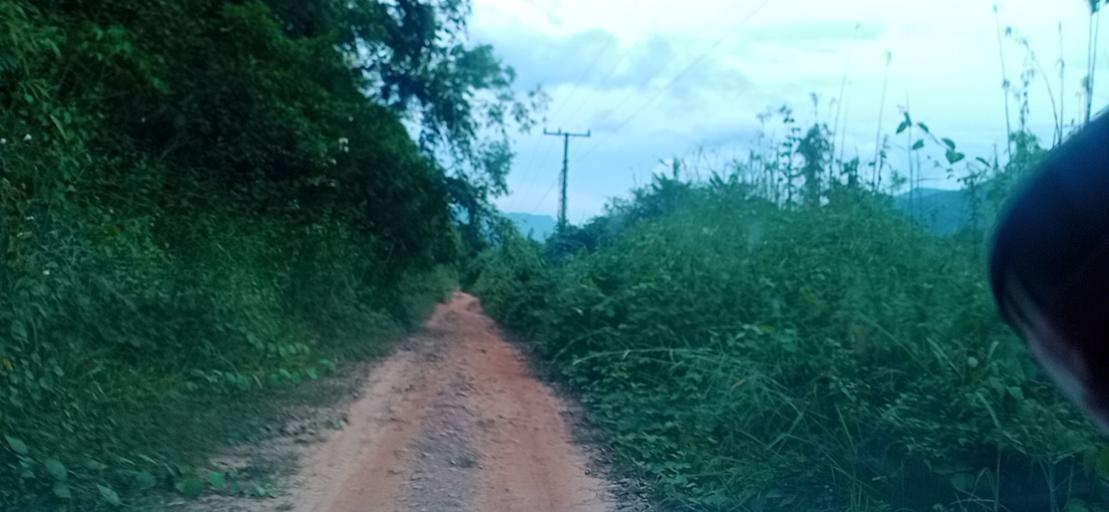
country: TH
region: Changwat Bueng Kan
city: Pak Khat
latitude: 18.5624
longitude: 103.2703
